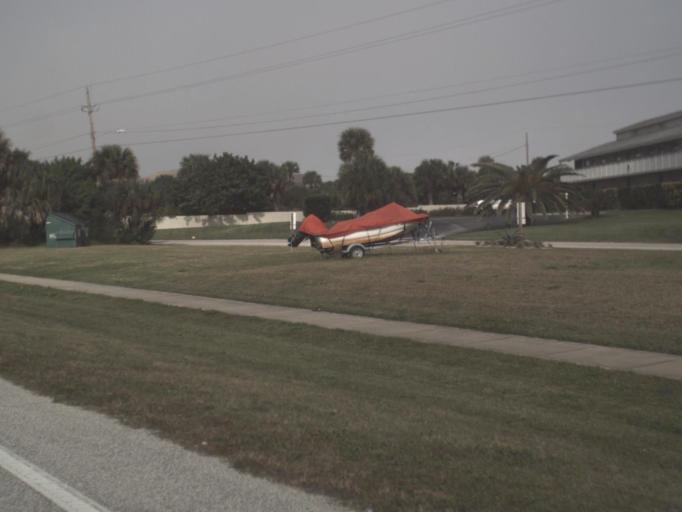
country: US
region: Florida
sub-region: Volusia County
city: Edgewater
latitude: 28.9813
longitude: -80.8618
